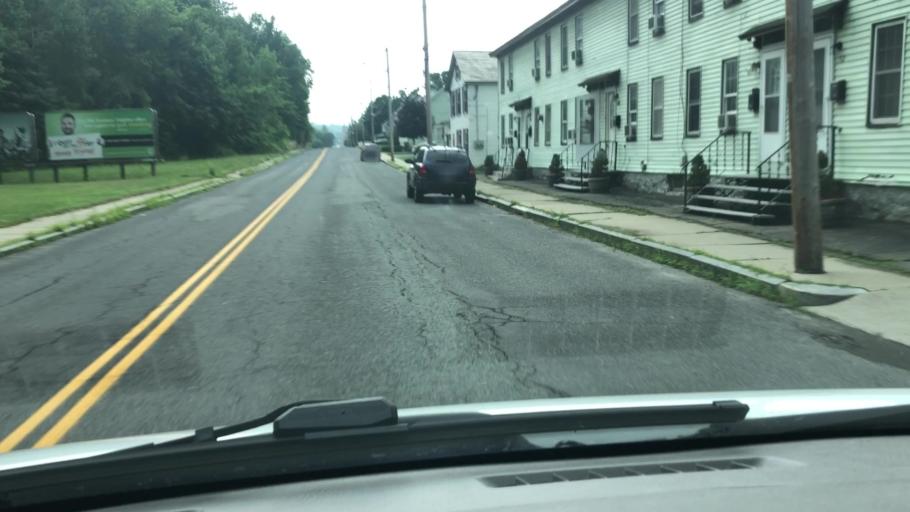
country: US
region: Massachusetts
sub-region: Berkshire County
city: Adams
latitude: 42.6355
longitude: -73.1088
